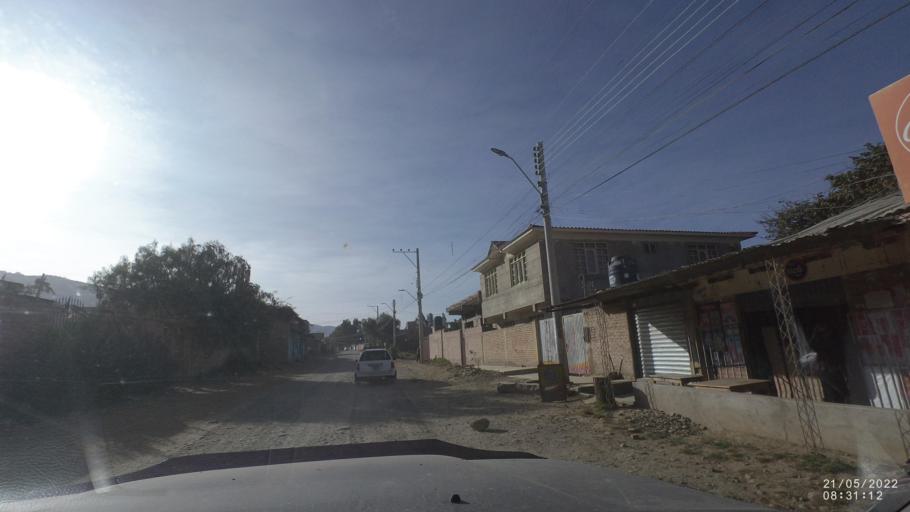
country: BO
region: Cochabamba
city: Cochabamba
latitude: -17.3850
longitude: -66.0566
